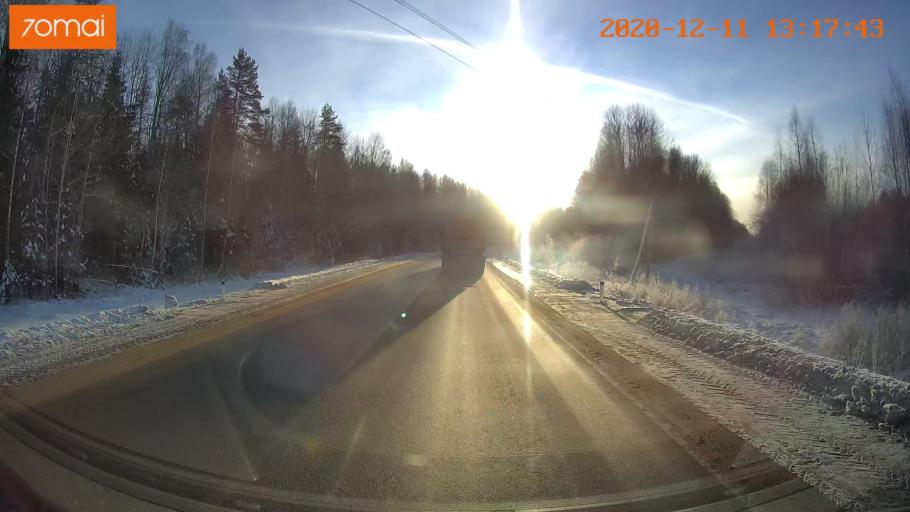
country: RU
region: Kostroma
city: Susanino
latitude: 58.0921
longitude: 41.5811
